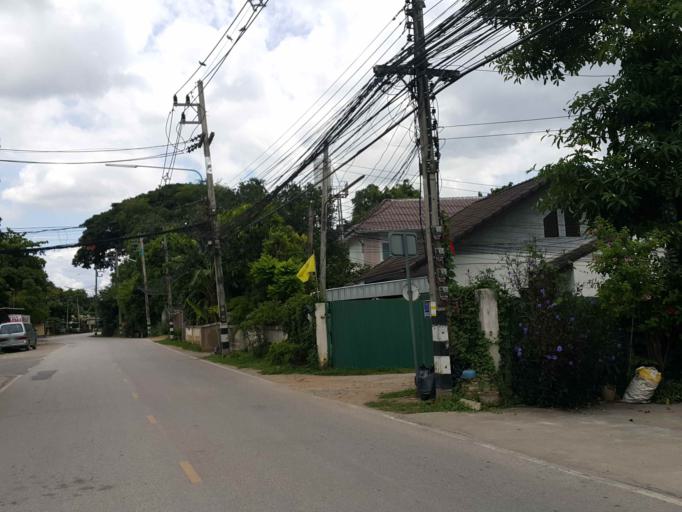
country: TH
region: Chiang Mai
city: Chiang Mai
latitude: 18.8189
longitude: 99.0007
